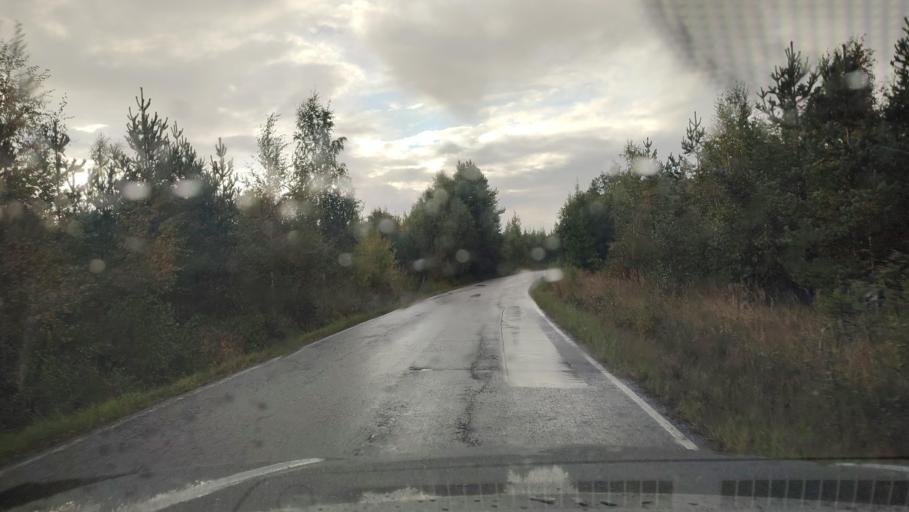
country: FI
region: Southern Ostrobothnia
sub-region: Suupohja
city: Karijoki
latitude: 62.3291
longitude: 21.6518
